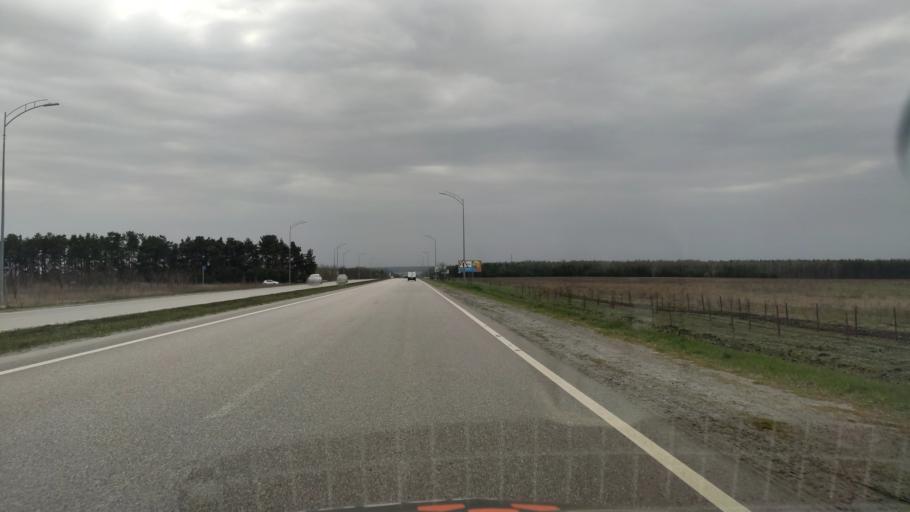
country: RU
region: Belgorod
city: Staryy Oskol
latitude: 51.3735
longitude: 37.8486
